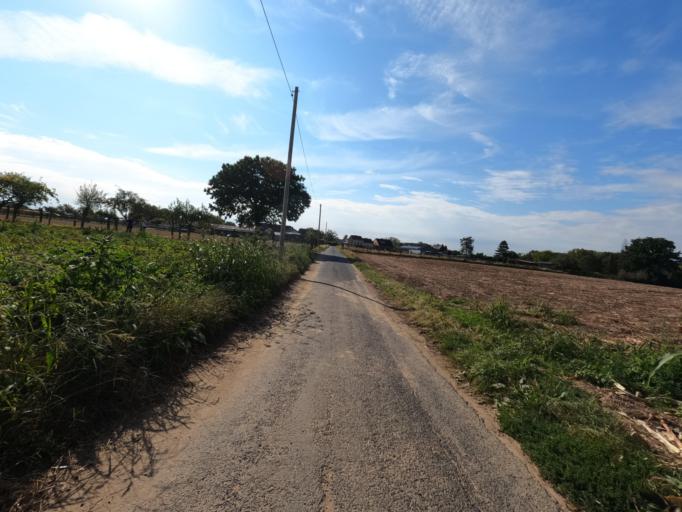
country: DE
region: North Rhine-Westphalia
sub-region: Regierungsbezirk Koln
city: Wassenberg
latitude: 51.0844
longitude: 6.1596
